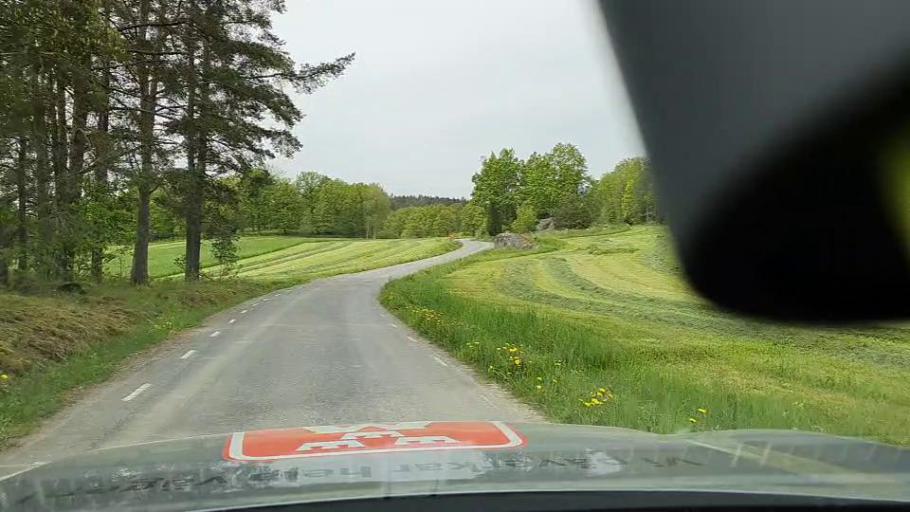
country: SE
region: Soedermanland
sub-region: Flens Kommun
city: Halleforsnas
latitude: 59.1012
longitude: 16.4790
